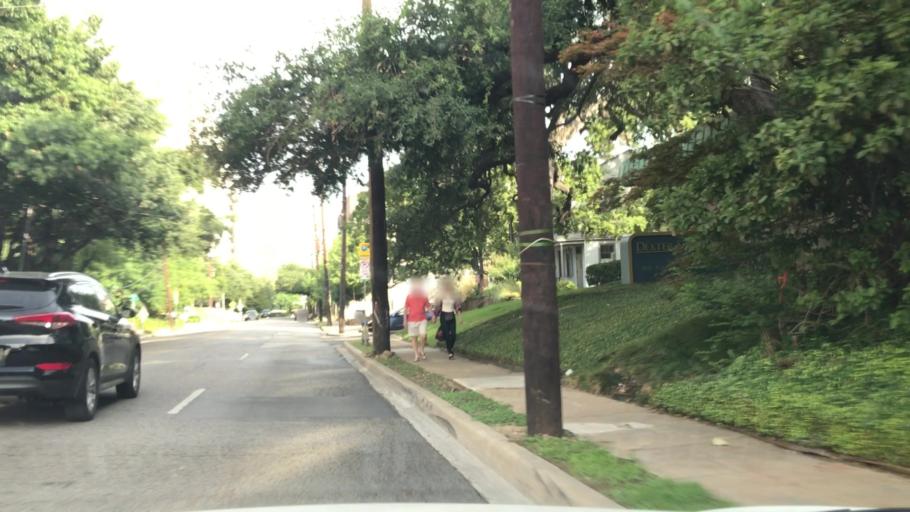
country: US
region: Texas
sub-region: Dallas County
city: Dallas
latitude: 32.8078
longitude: -96.8071
